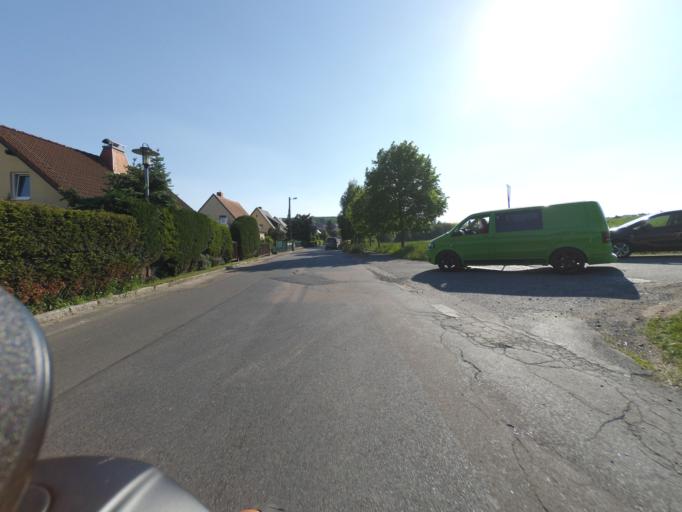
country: DE
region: Saxony
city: Bannewitz
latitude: 50.9692
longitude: 13.7182
